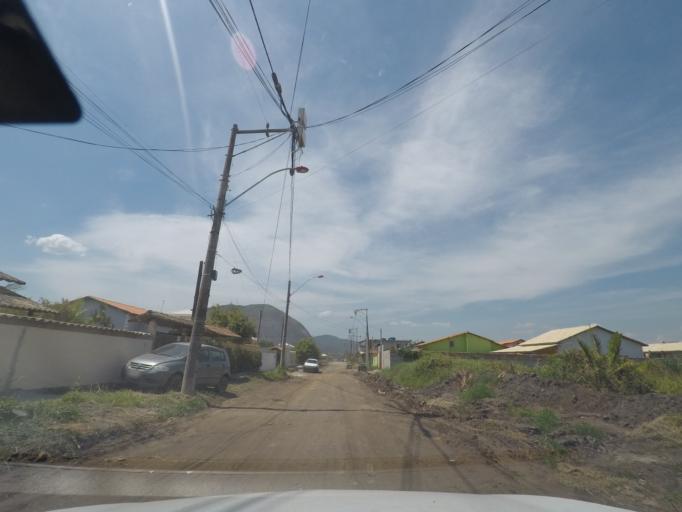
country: BR
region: Rio de Janeiro
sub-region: Marica
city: Marica
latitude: -22.9607
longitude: -42.9559
